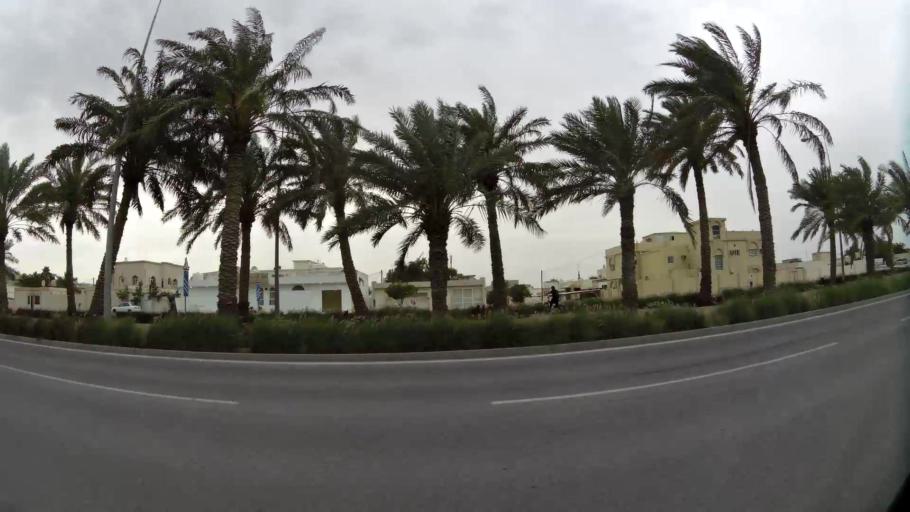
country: QA
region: Baladiyat ad Dawhah
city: Doha
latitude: 25.3098
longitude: 51.4876
